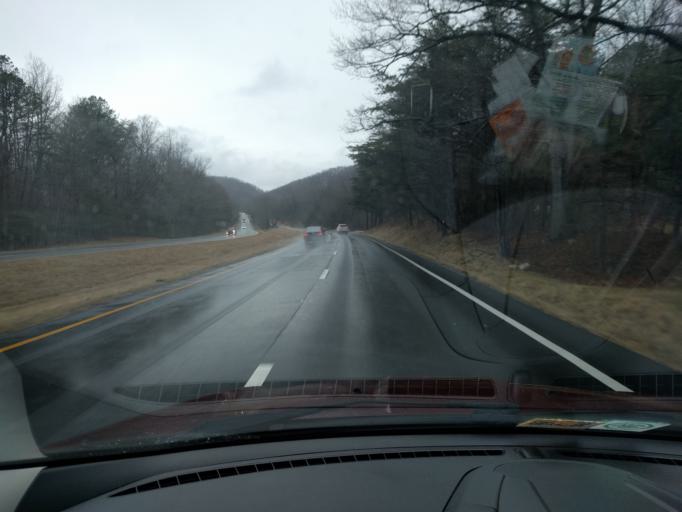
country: US
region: Virginia
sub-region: Montgomery County
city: Blacksburg
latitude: 37.2861
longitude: -80.4642
